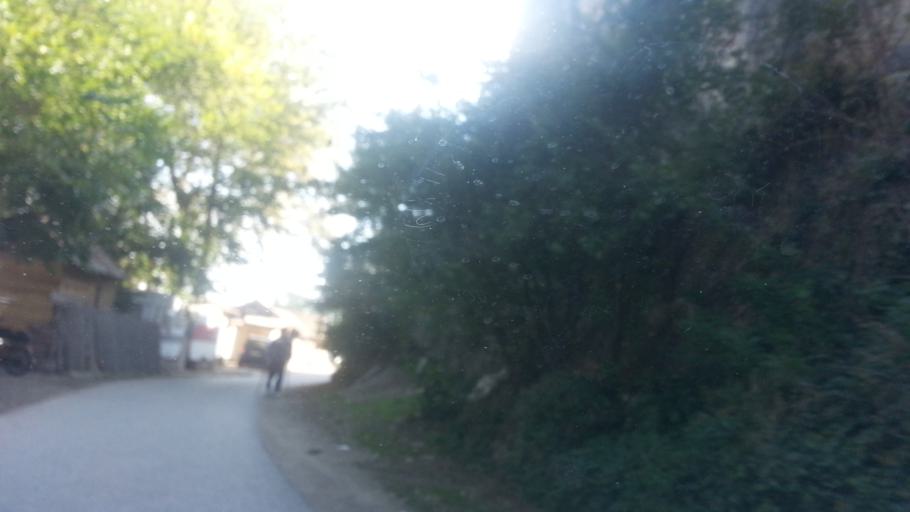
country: RS
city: Novi Slankamen
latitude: 45.1458
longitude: 20.2550
